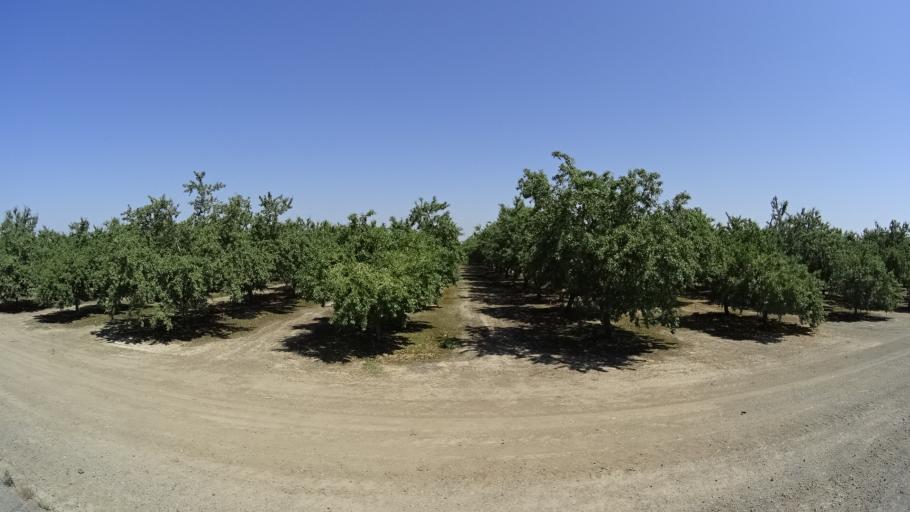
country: US
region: California
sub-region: Kings County
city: Armona
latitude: 36.3718
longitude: -119.7355
